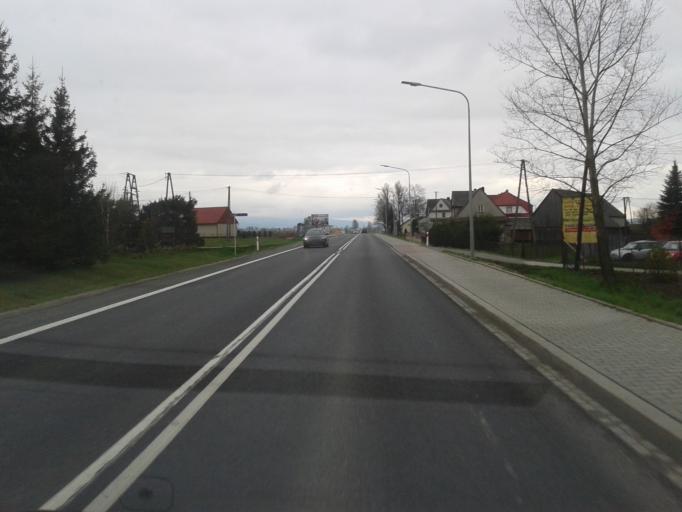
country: PL
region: Lesser Poland Voivodeship
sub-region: Powiat nowotarski
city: Jablonka
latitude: 49.4578
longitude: 19.6899
